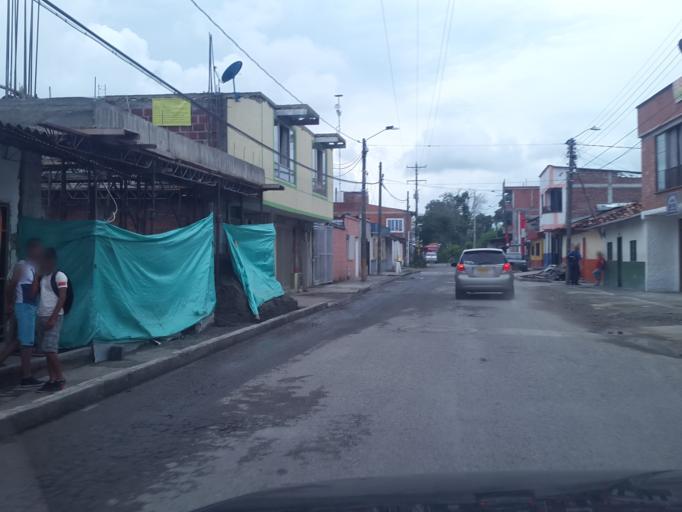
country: CO
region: Quindio
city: La Tebaida
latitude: 4.5100
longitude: -75.7859
